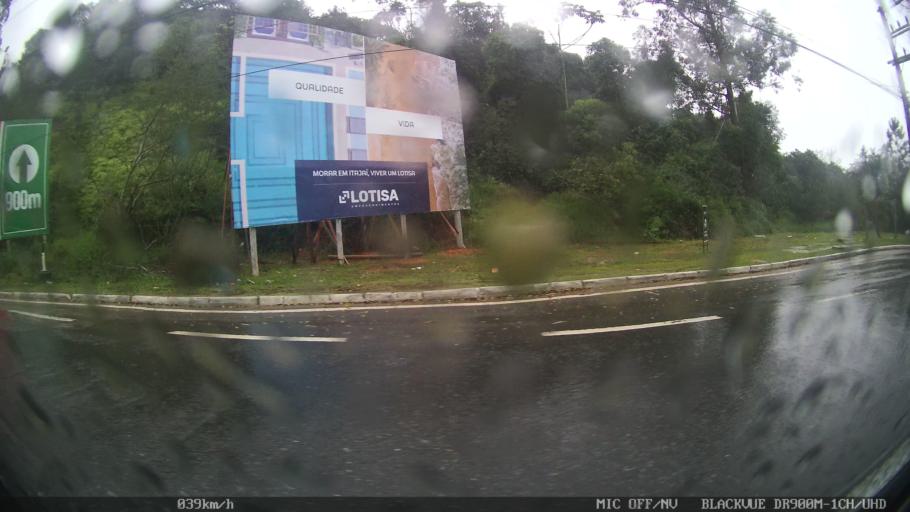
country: BR
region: Santa Catarina
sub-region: Itajai
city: Itajai
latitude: -26.9378
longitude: -48.6416
